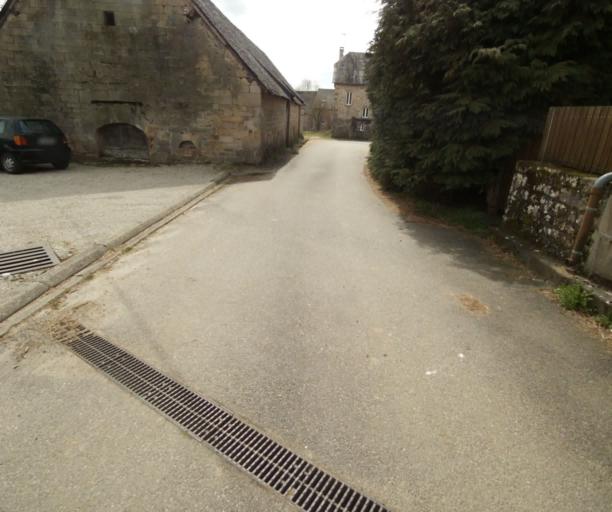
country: FR
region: Limousin
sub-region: Departement de la Correze
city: Correze
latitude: 45.3878
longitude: 1.9621
